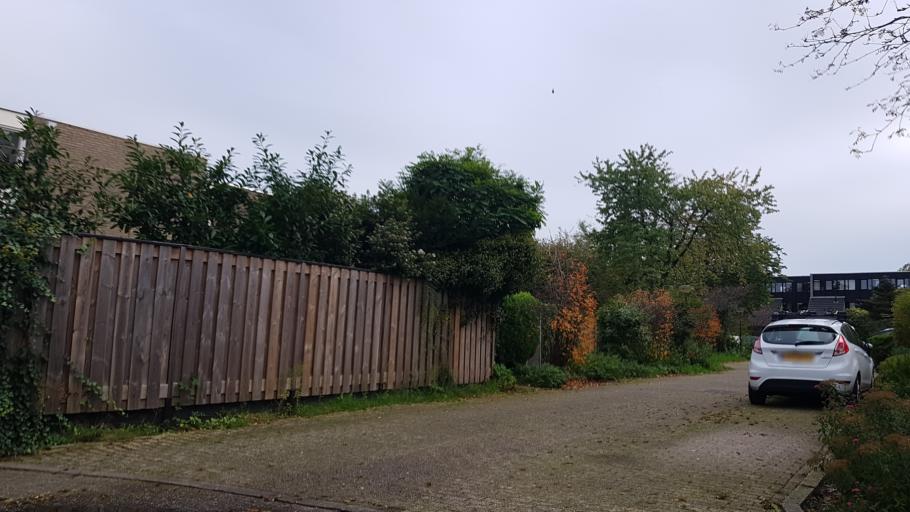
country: NL
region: Gelderland
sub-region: Gemeente Apeldoorn
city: Apeldoorn
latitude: 52.2015
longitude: 5.9824
